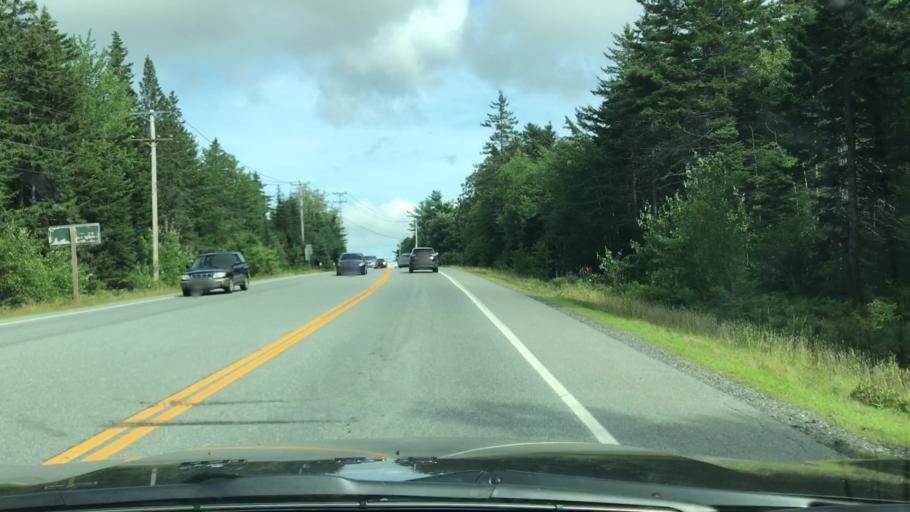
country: US
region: Maine
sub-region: Hancock County
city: Trenton
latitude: 44.4205
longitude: -68.3602
